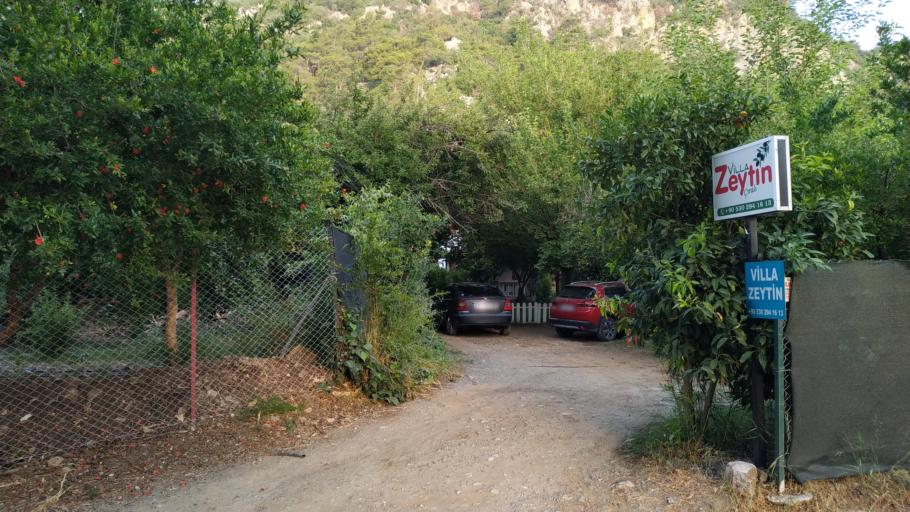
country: TR
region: Antalya
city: Tekirova
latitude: 36.4110
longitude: 30.4758
